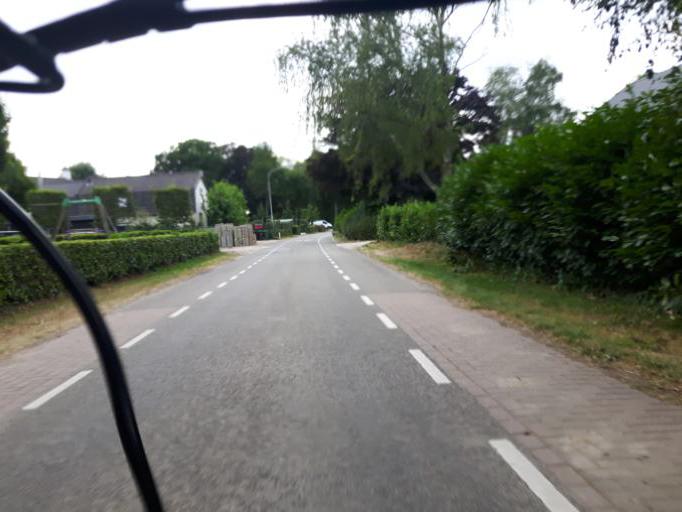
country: NL
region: Gelderland
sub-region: Gemeente Tiel
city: Tiel
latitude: 51.8807
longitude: 5.3772
